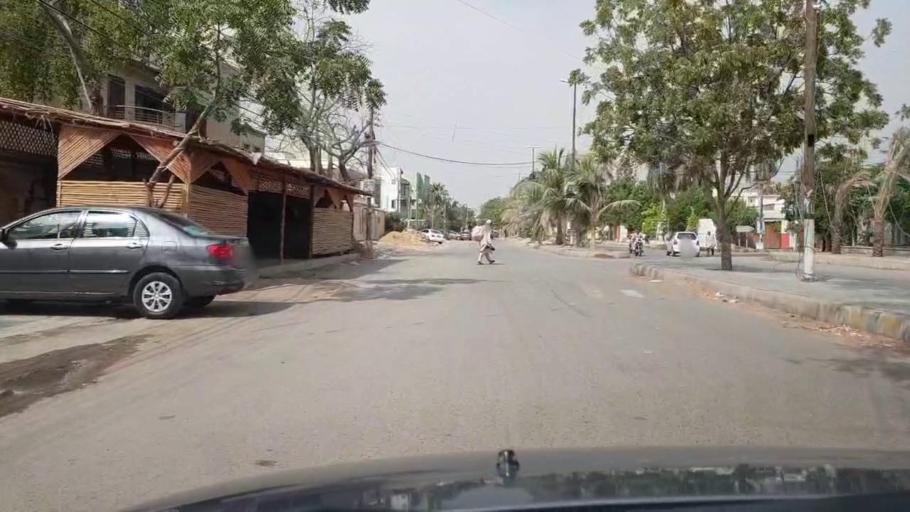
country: PK
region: Sindh
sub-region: Karachi District
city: Karachi
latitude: 24.8734
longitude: 67.0872
